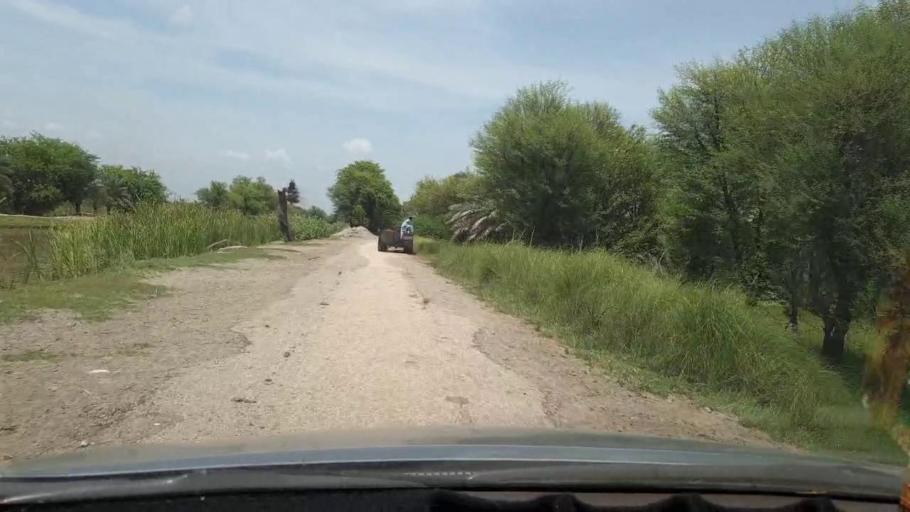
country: PK
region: Sindh
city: Khairpur
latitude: 27.4473
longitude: 68.7966
